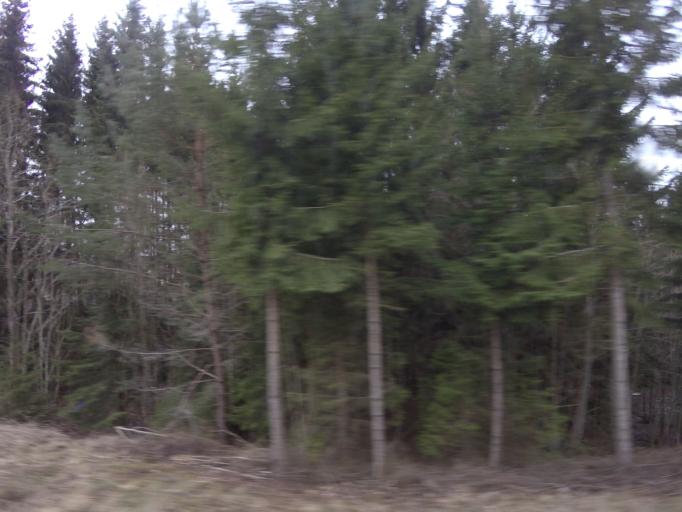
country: NO
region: Akershus
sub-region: Enebakk
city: Kirkebygda
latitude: 59.7708
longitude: 11.2781
